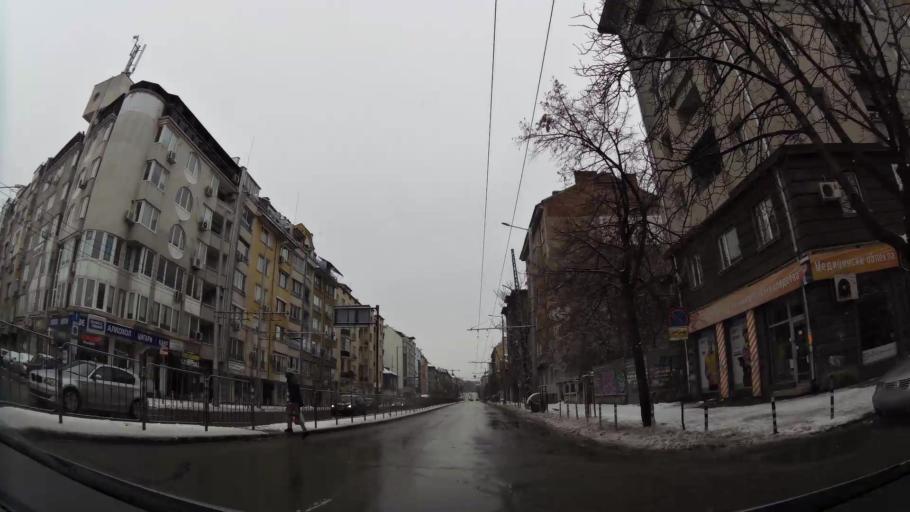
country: BG
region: Sofia-Capital
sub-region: Stolichna Obshtina
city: Sofia
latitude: 42.7041
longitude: 23.3330
